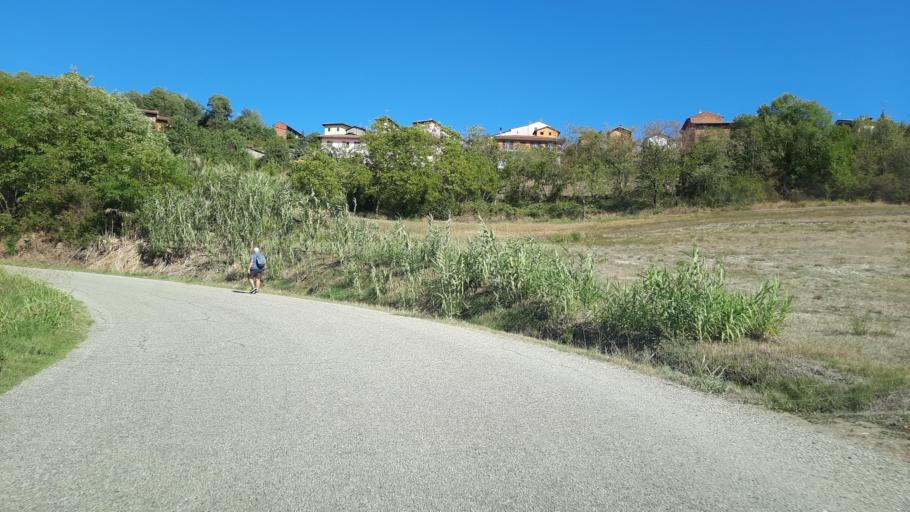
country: IT
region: Piedmont
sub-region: Provincia di Alessandria
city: Cuccaro Monferrato
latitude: 44.9945
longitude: 8.4535
